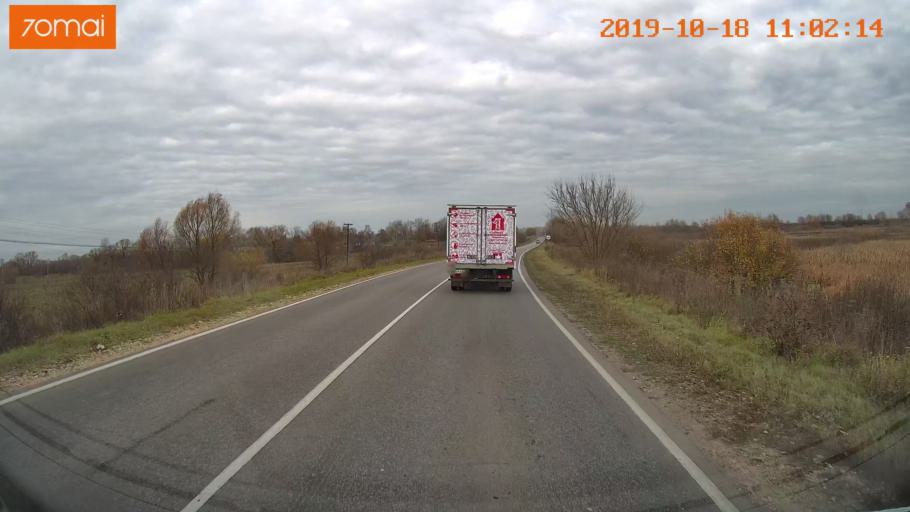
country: RU
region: Tula
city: Yepifan'
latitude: 53.8629
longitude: 38.5455
